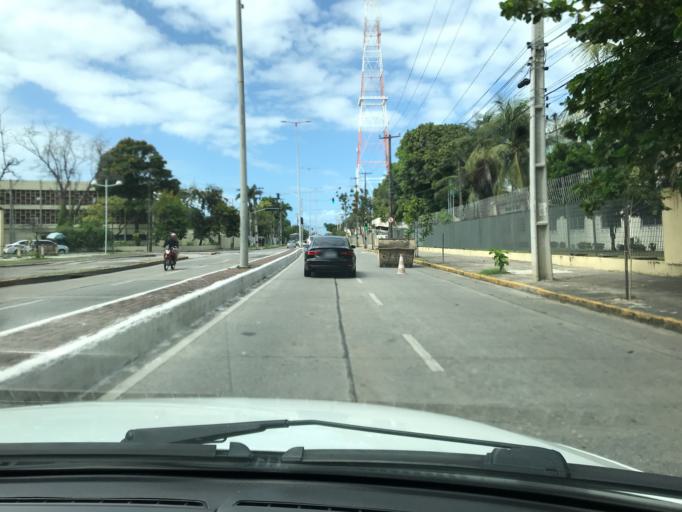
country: BR
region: Pernambuco
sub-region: Recife
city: Recife
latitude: -8.0477
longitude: -34.8767
